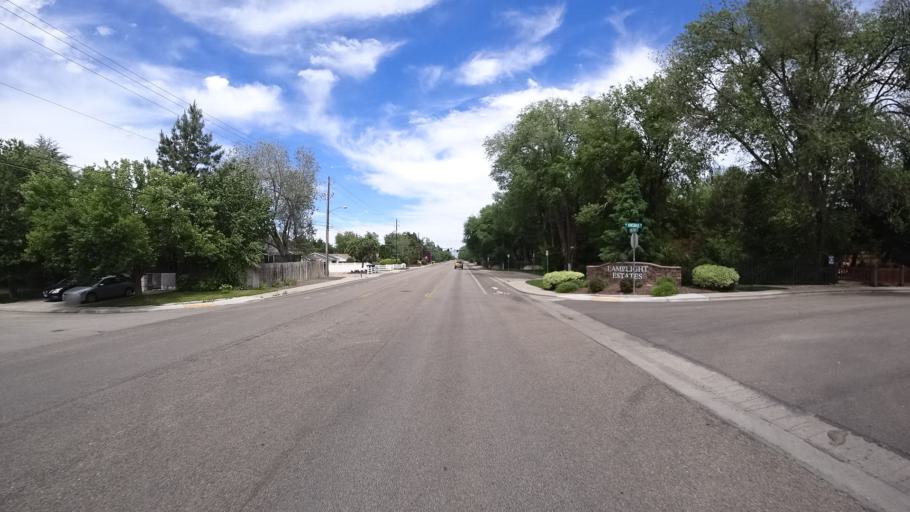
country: US
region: Idaho
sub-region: Ada County
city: Eagle
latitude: 43.6396
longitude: -116.3142
